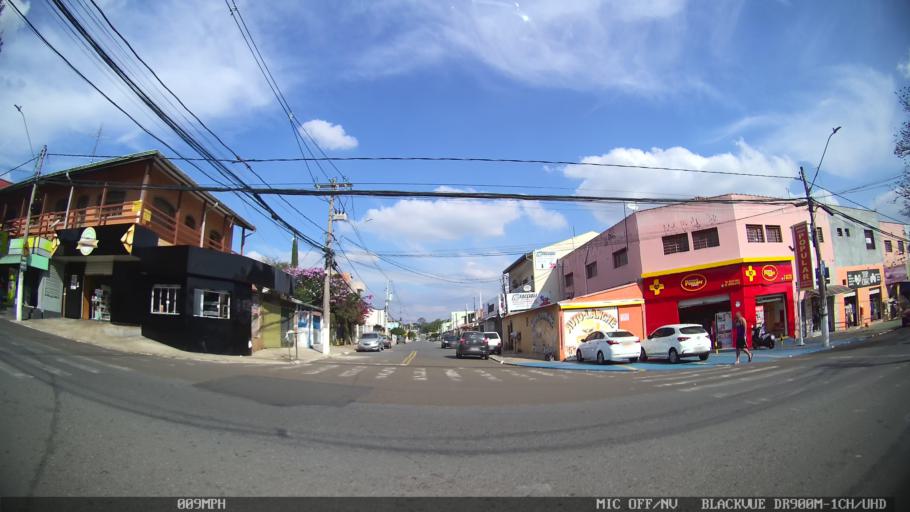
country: BR
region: Sao Paulo
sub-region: Hortolandia
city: Hortolandia
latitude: -22.8996
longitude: -47.2329
